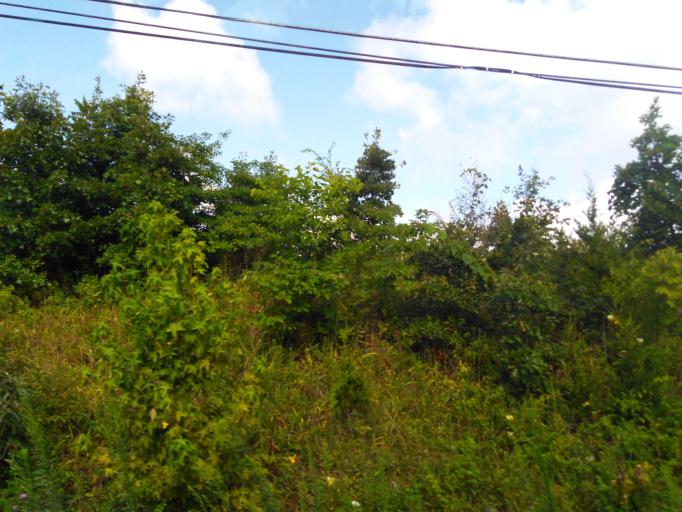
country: US
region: Missouri
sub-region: Jefferson County
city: Hillsboro
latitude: 38.2467
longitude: -90.5580
